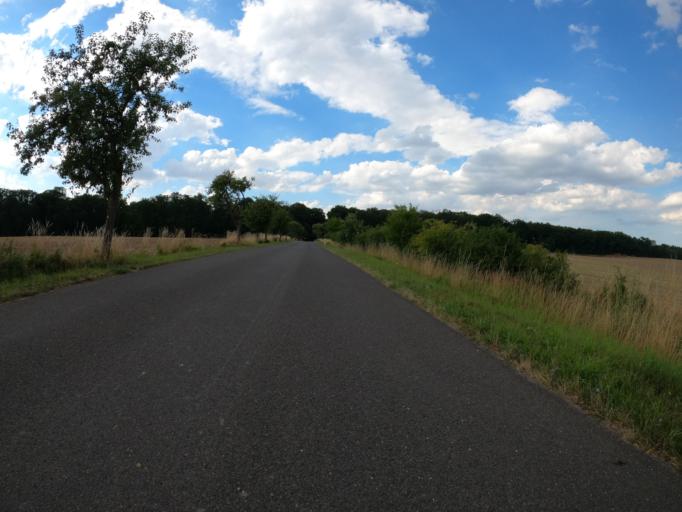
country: DE
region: Mecklenburg-Vorpommern
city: Woldegk
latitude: 53.4278
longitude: 13.6024
